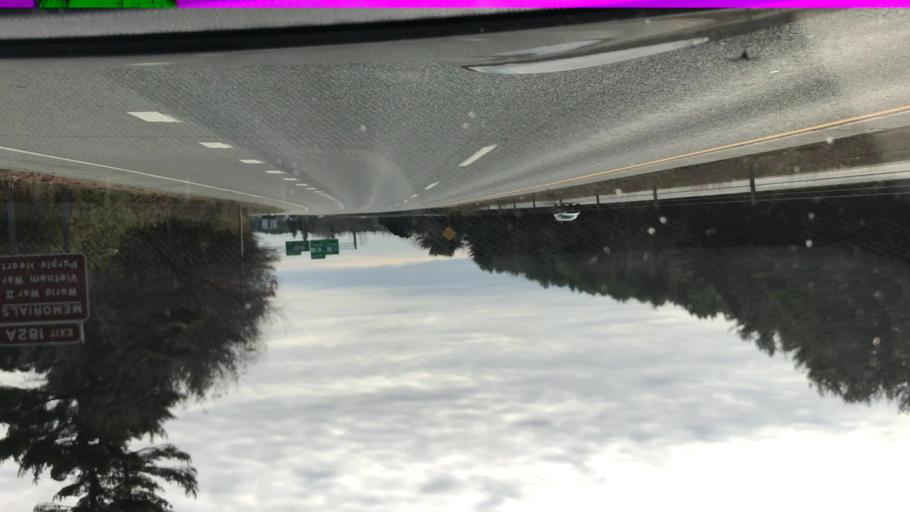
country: US
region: Maine
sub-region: Penobscot County
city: Bangor
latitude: 44.7946
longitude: -68.8035
